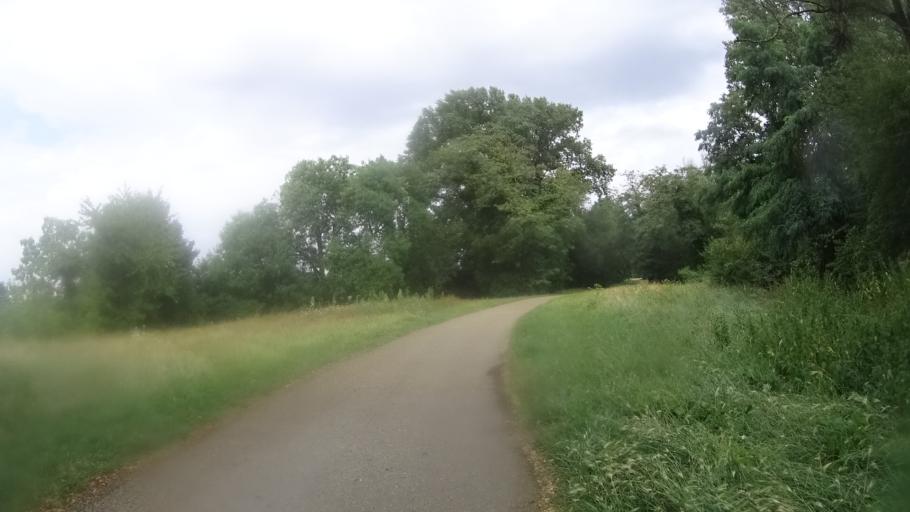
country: FR
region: Centre
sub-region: Departement du Loiret
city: Saint-Jean-le-Blanc
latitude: 47.8981
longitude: 1.9335
